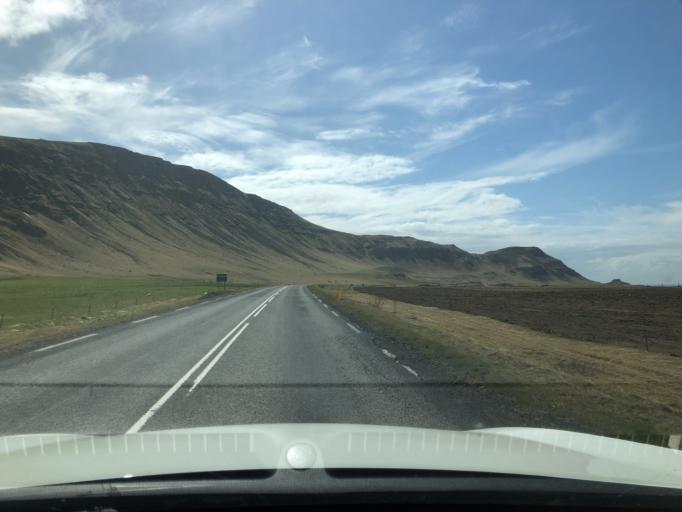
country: IS
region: Capital Region
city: Mosfellsbaer
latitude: 64.2976
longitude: -21.7915
